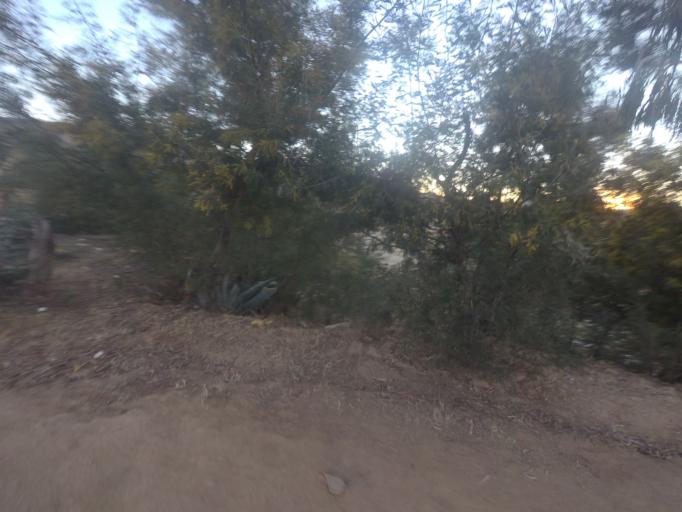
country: LS
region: Maseru
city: Nako
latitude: -29.4444
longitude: 27.7119
